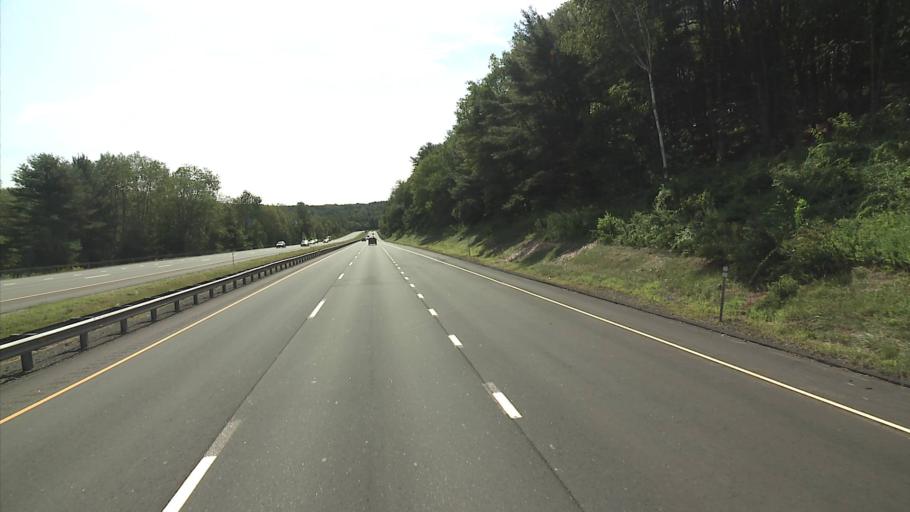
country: US
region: Connecticut
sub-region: Hartford County
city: Terramuggus
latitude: 41.6078
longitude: -72.4296
